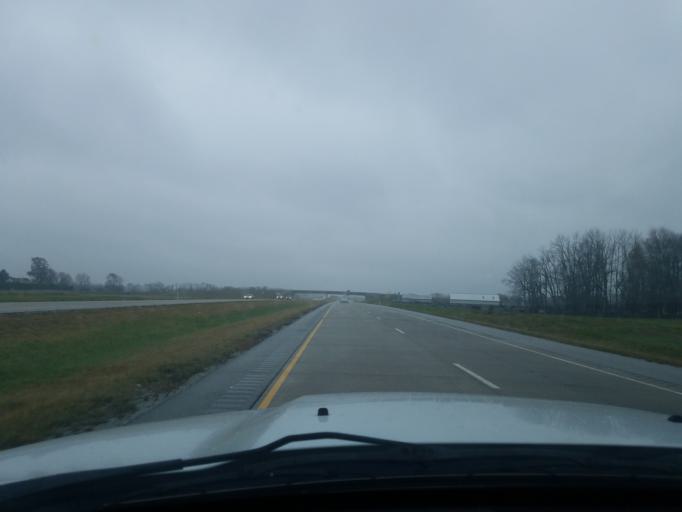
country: US
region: Indiana
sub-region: Howard County
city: Kokomo
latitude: 40.4879
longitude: -86.0867
